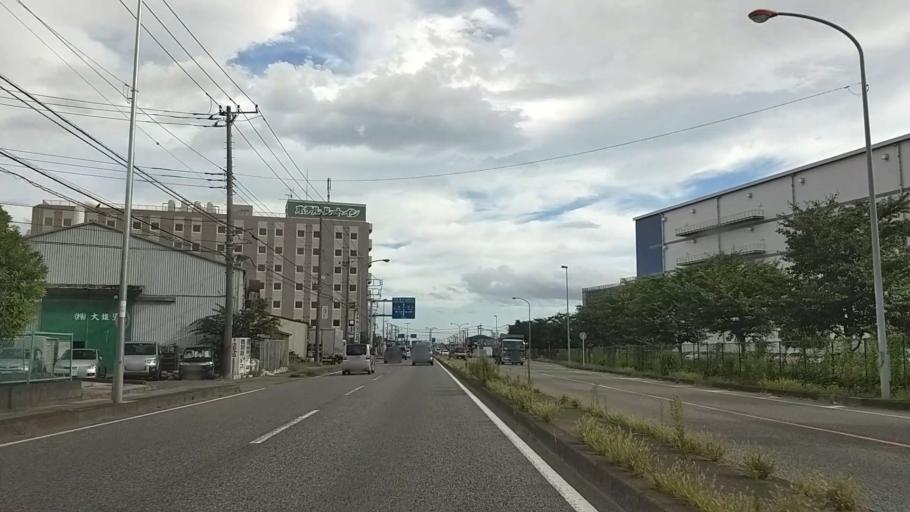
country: JP
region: Kanagawa
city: Zama
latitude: 35.5603
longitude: 139.3468
